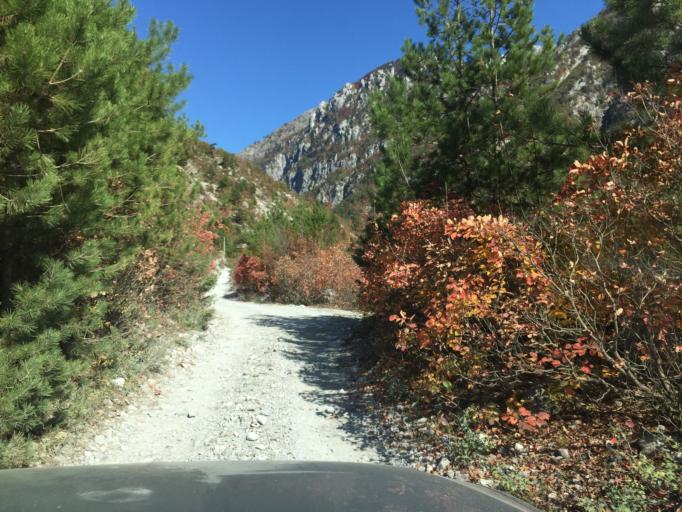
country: AL
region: Shkoder
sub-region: Rrethi i Shkodres
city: Nicaj-Shale
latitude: 42.3594
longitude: 19.7828
